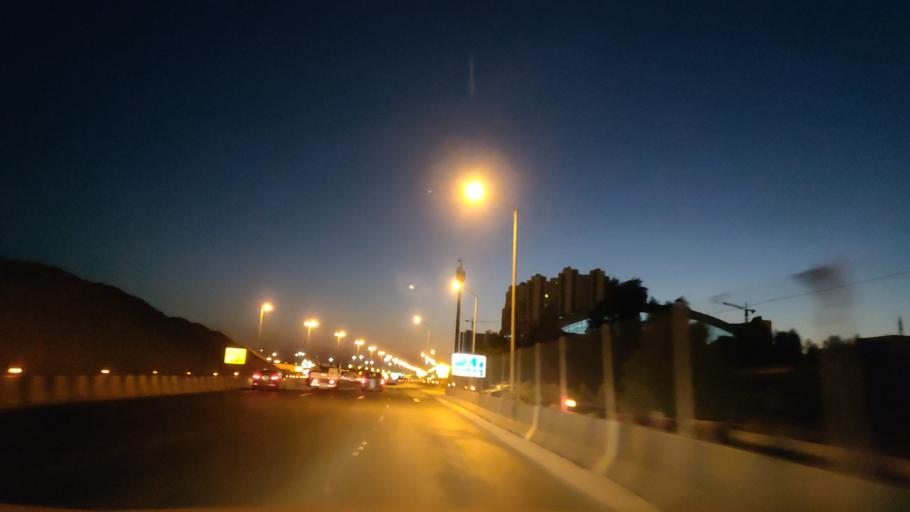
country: KW
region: Mubarak al Kabir
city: Sabah as Salim
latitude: 29.2651
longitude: 48.0716
